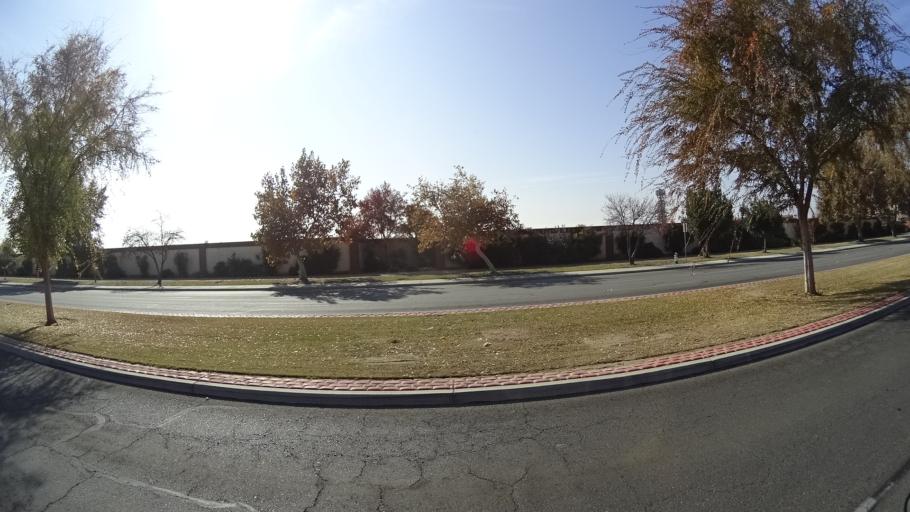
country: US
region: California
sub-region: Kern County
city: Rosedale
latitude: 35.3533
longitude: -119.1351
